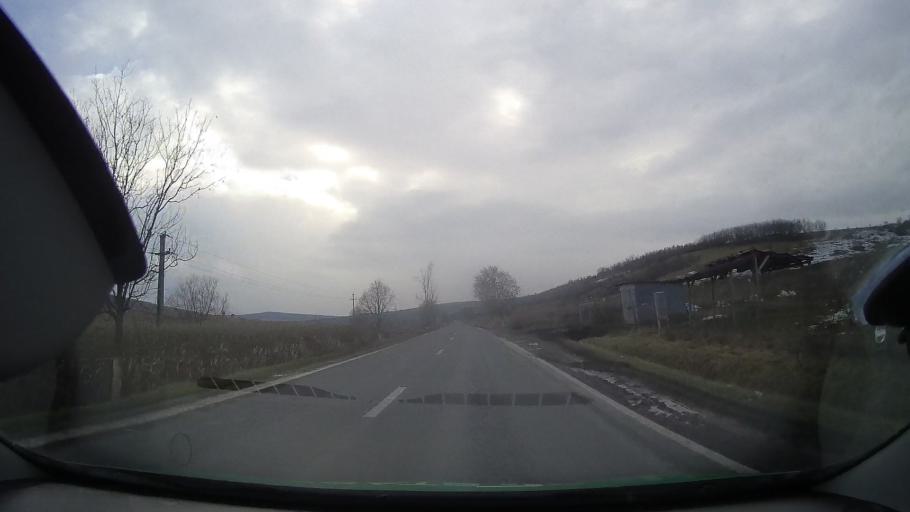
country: RO
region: Mures
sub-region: Comuna Cucerdea
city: Cucerdea
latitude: 46.3897
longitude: 24.2564
